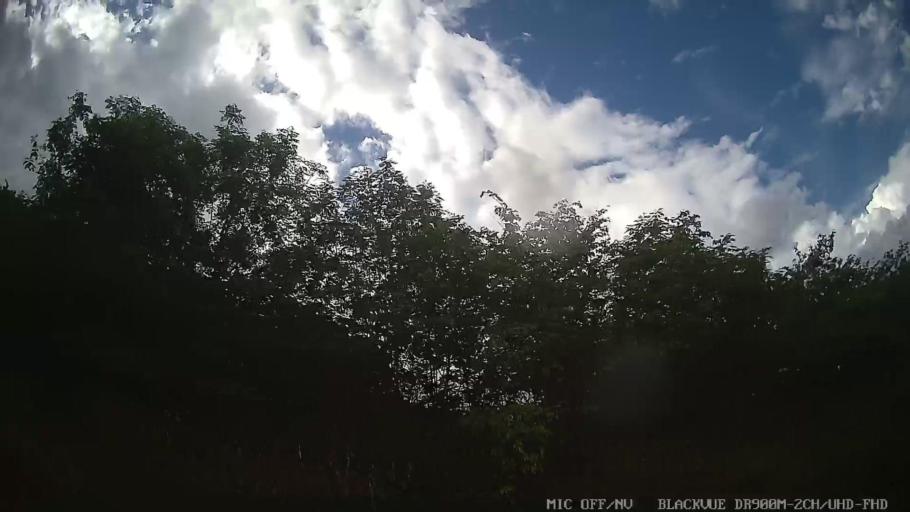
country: BR
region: Sao Paulo
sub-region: Jaguariuna
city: Jaguariuna
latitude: -22.6667
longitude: -47.0578
